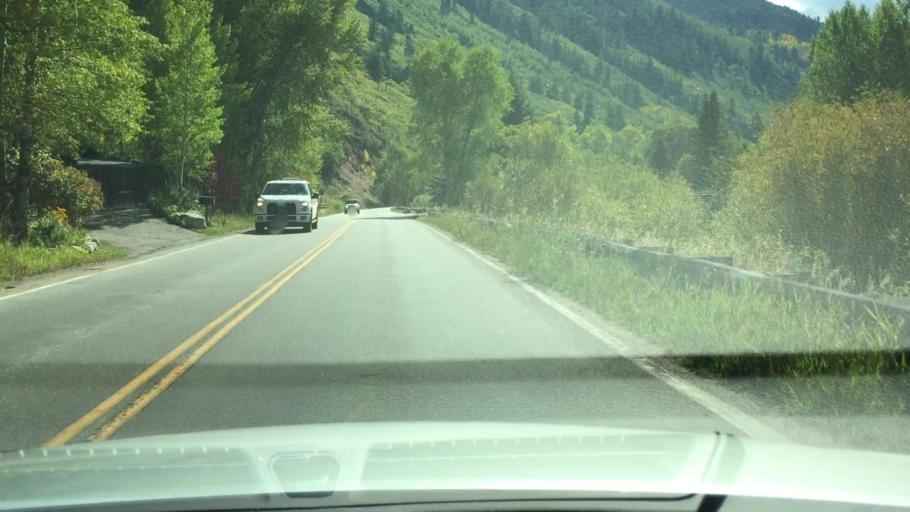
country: US
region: Colorado
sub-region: Pitkin County
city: Aspen
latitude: 39.1780
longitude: -106.7989
